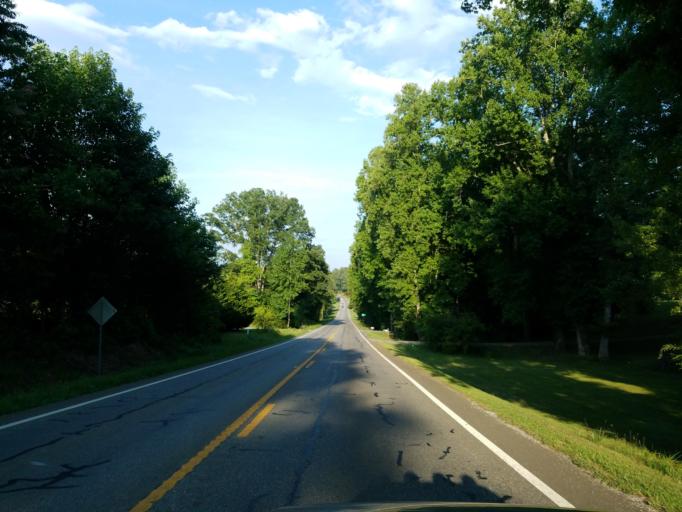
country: US
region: Georgia
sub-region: Pickens County
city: Jasper
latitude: 34.5110
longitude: -84.5546
